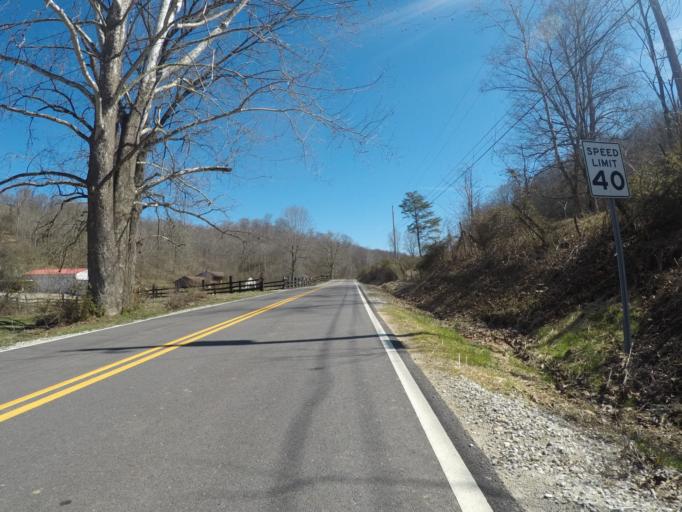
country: US
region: Ohio
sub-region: Lawrence County
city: South Point
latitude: 38.4656
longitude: -82.5686
